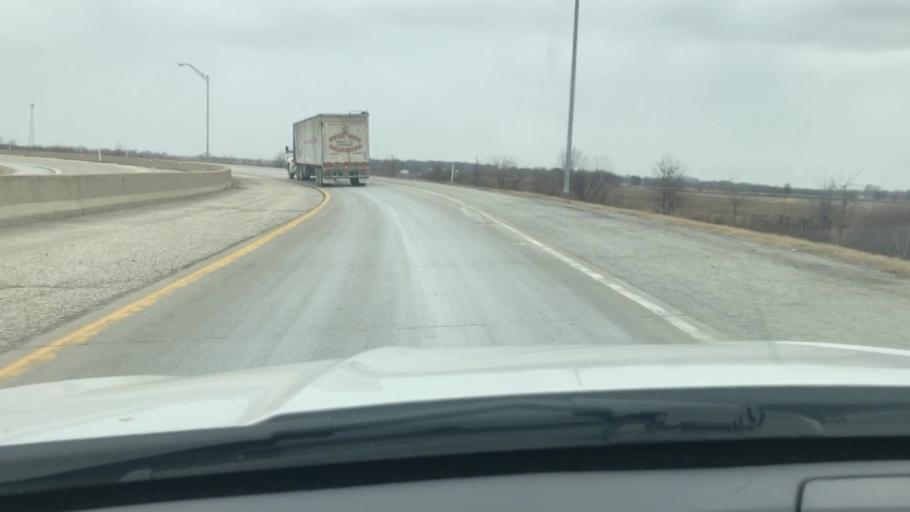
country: US
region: Indiana
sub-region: Tippecanoe County
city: Dayton
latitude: 40.3766
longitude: -86.7816
